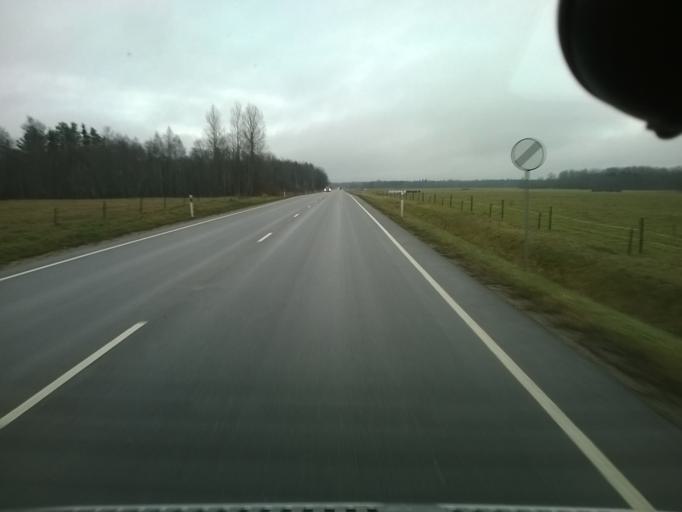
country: EE
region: Laeaene
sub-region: Ridala Parish
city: Uuemoisa
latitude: 58.9635
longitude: 23.8257
